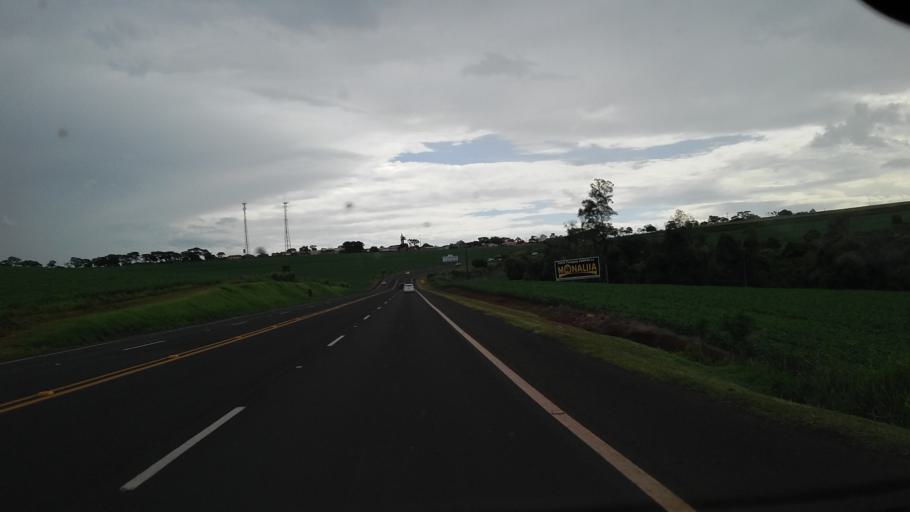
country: BR
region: Parana
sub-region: Mandaguari
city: Mandaguari
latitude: -23.4739
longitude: -51.5809
